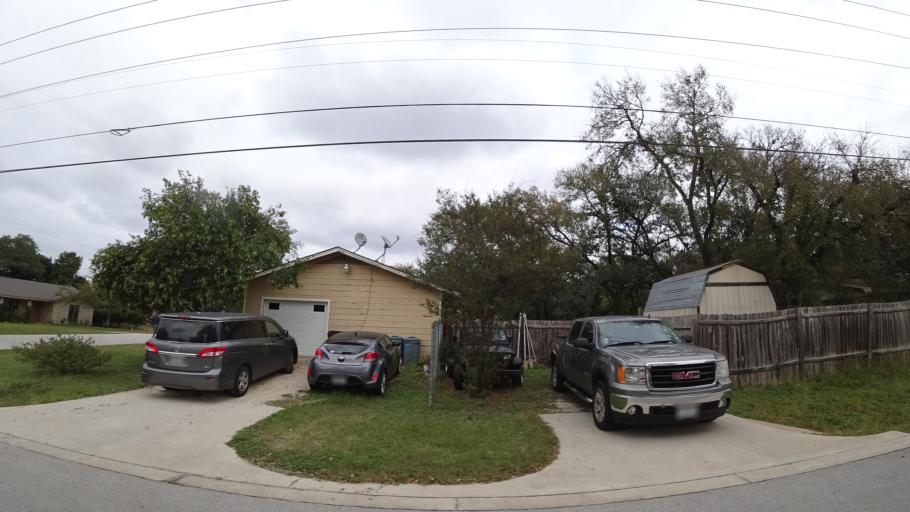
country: US
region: Texas
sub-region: Williamson County
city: Round Rock
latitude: 30.5107
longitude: -97.6932
